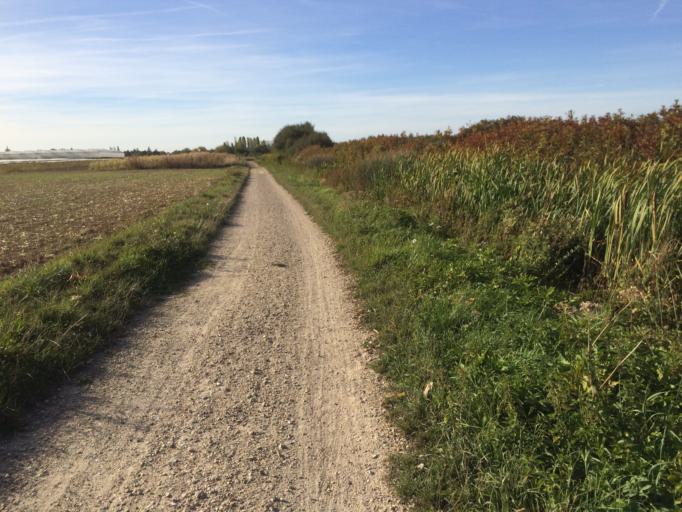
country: FR
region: Ile-de-France
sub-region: Departement de l'Essonne
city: Vauhallan
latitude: 48.7292
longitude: 2.1912
